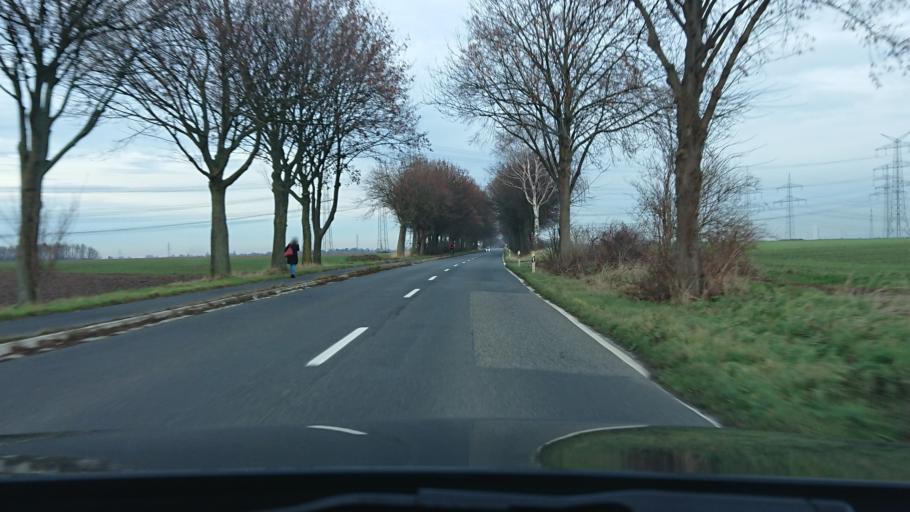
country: DE
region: North Rhine-Westphalia
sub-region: Regierungsbezirk Koln
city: Pulheim
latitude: 51.0007
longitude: 6.7445
